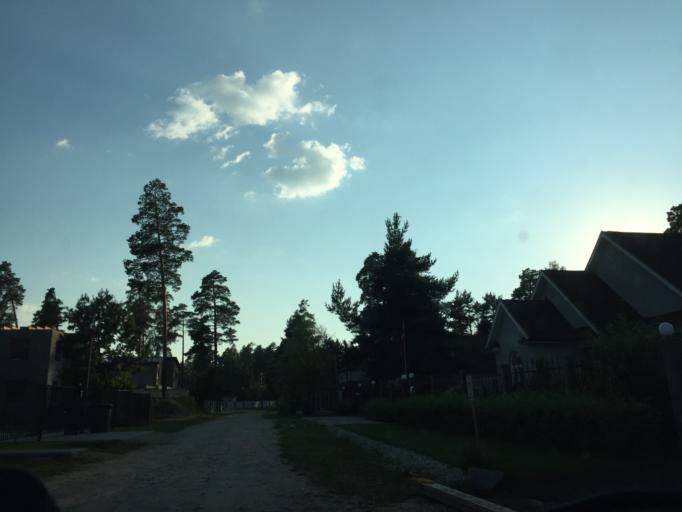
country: LV
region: Riga
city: Bergi
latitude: 56.9785
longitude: 24.3770
